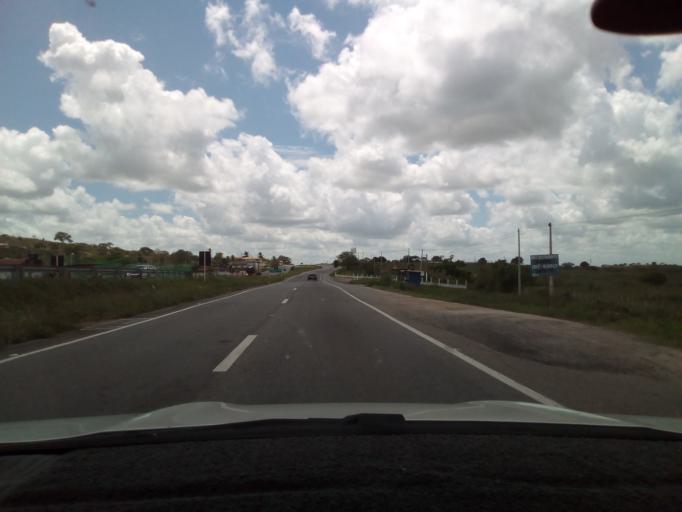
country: BR
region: Paraiba
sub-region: Gurinhem
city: Gurinhem
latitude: -7.1748
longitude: -35.4027
